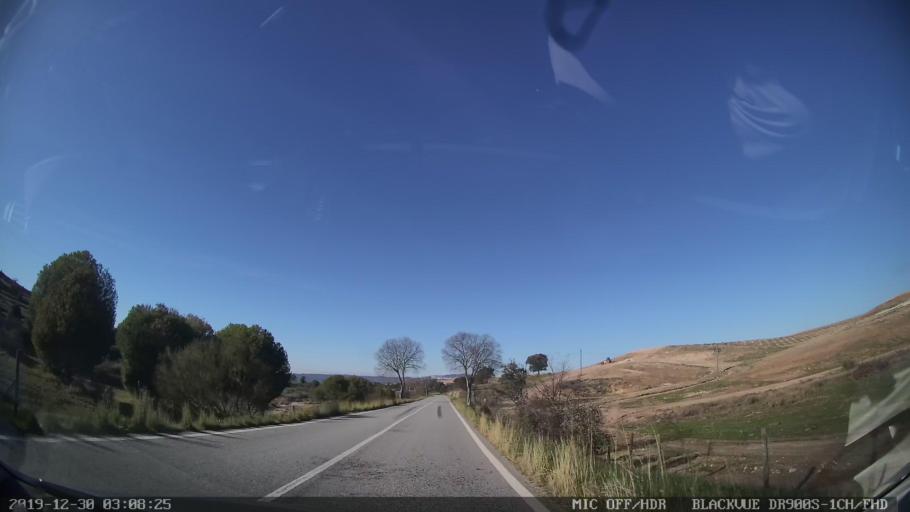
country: PT
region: Castelo Branco
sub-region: Idanha-A-Nova
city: Idanha-a-Nova
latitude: 39.8808
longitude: -7.1966
